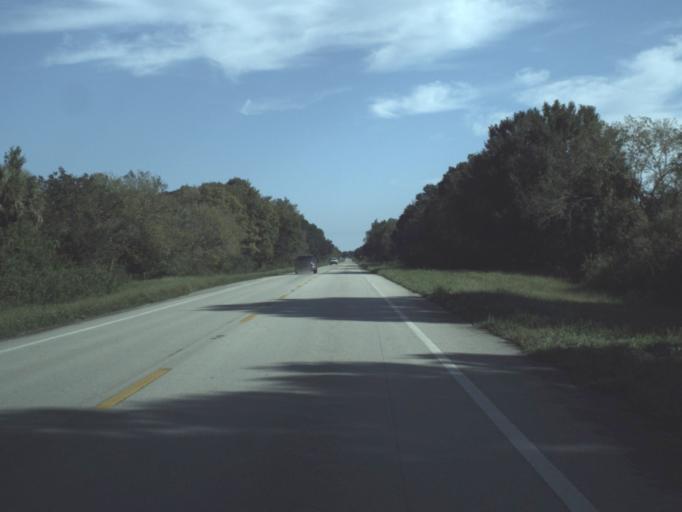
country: US
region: Florida
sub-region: Okeechobee County
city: Cypress Quarters
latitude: 27.3582
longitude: -80.8201
